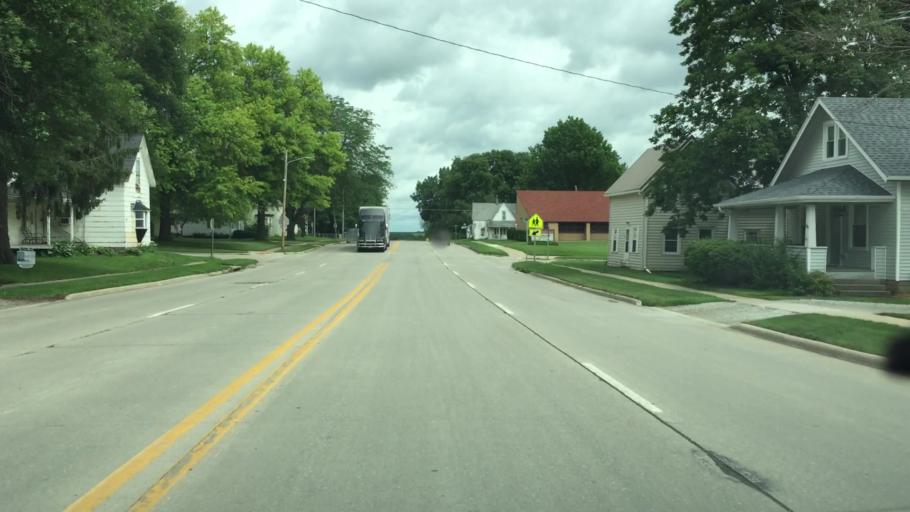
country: US
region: Iowa
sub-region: Jasper County
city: Monroe
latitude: 41.5236
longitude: -93.1018
